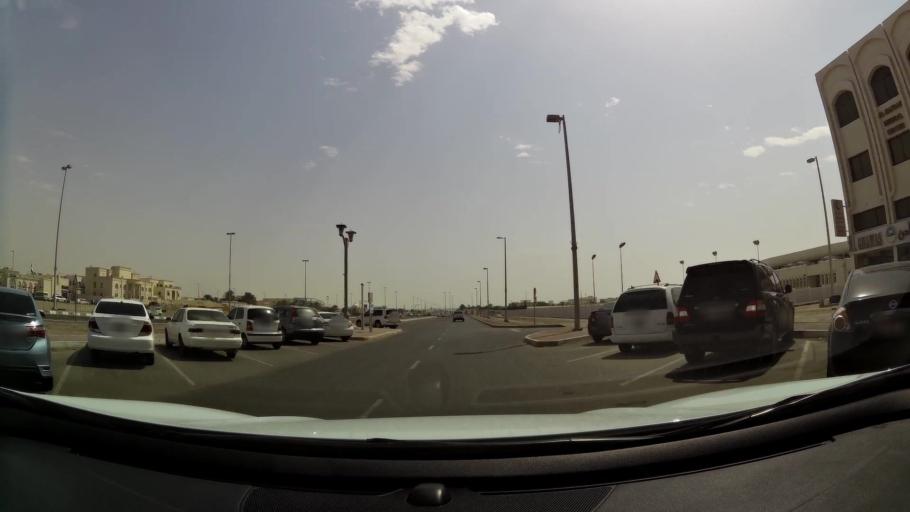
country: AE
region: Abu Dhabi
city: Abu Dhabi
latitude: 24.2959
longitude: 54.6403
